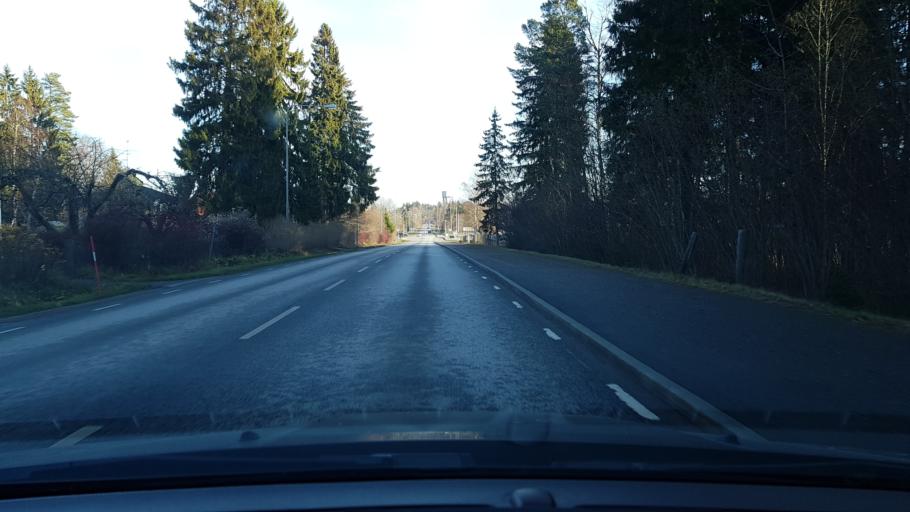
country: SE
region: Stockholm
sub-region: Norrtalje Kommun
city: Rimbo
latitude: 59.7402
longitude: 18.3414
